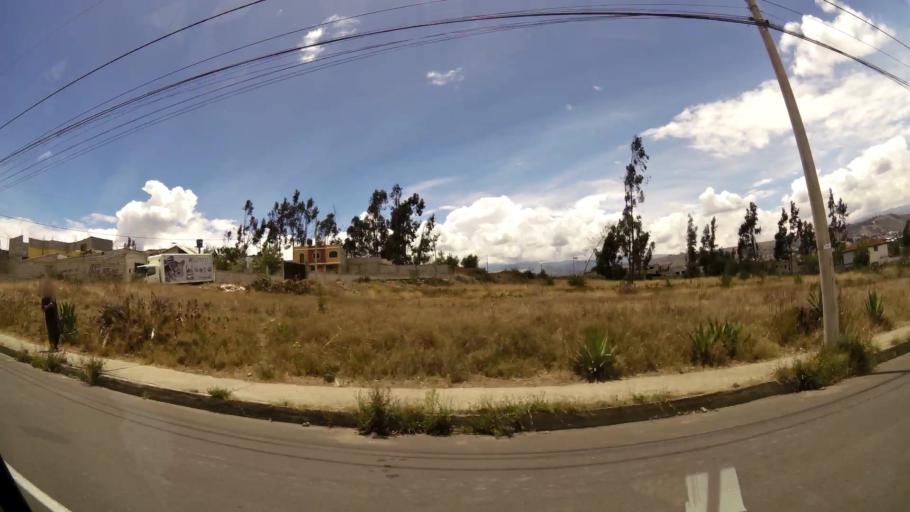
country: EC
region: Tungurahua
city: Ambato
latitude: -1.2731
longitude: -78.6036
